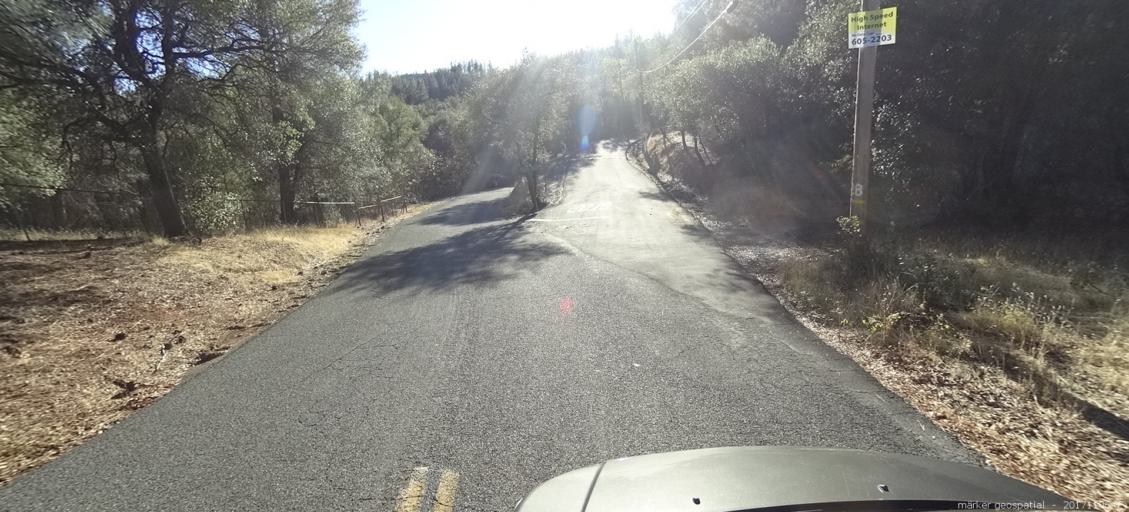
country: US
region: California
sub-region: Shasta County
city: Shasta
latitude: 40.5892
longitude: -122.4881
